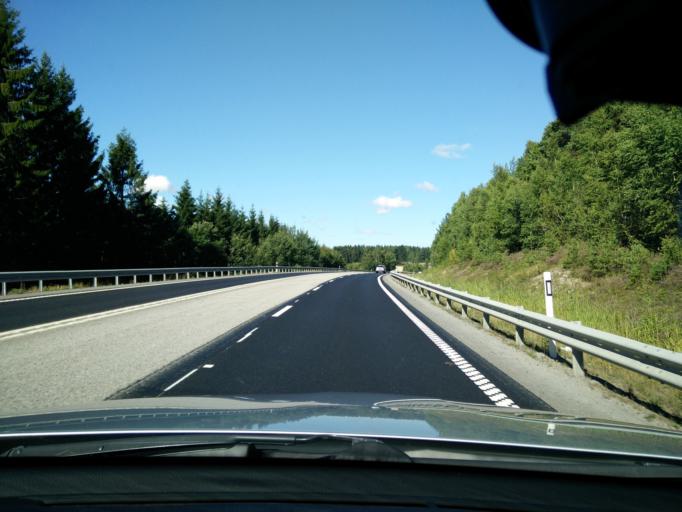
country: SE
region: Stockholm
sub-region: Lidingo
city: Lidingoe
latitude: 59.4532
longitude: 18.1809
